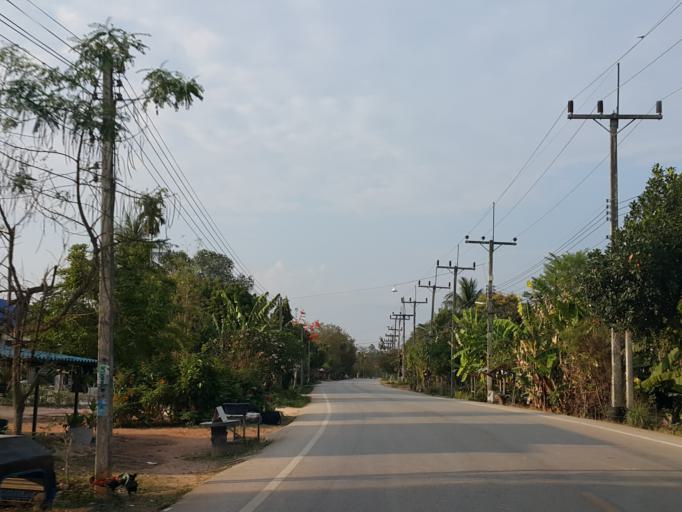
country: TH
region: Lampang
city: Chae Hom
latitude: 18.5488
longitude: 99.4769
